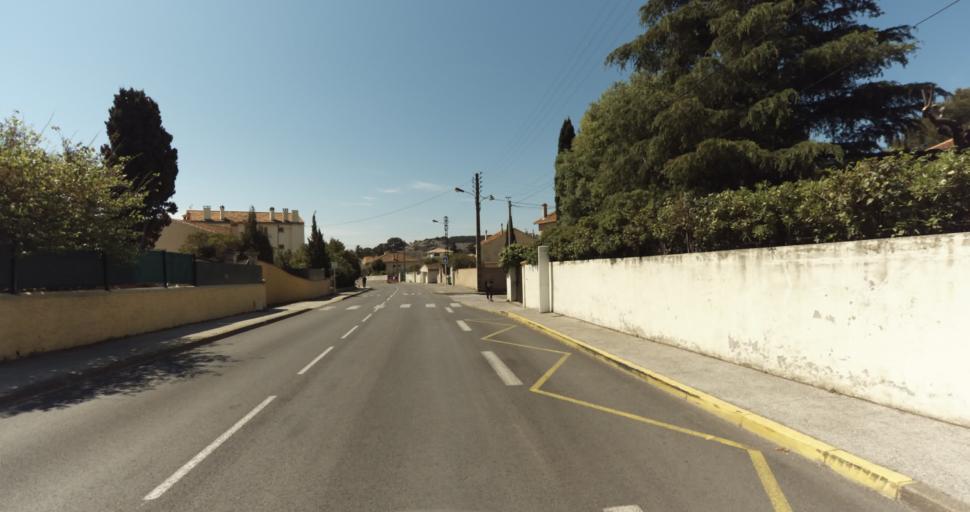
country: FR
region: Provence-Alpes-Cote d'Azur
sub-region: Departement du Var
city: Le Revest-les-Eaux
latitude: 43.1439
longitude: 5.9017
